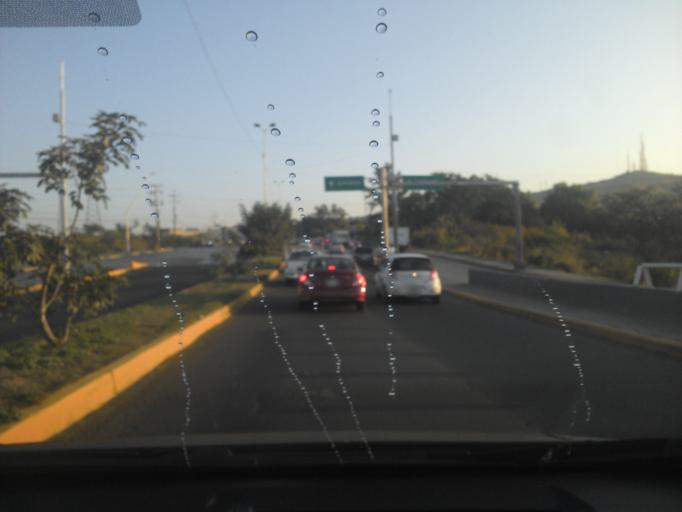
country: MX
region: Jalisco
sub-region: Tlajomulco de Zuniga
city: Altus Bosques
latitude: 20.5893
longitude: -103.3823
